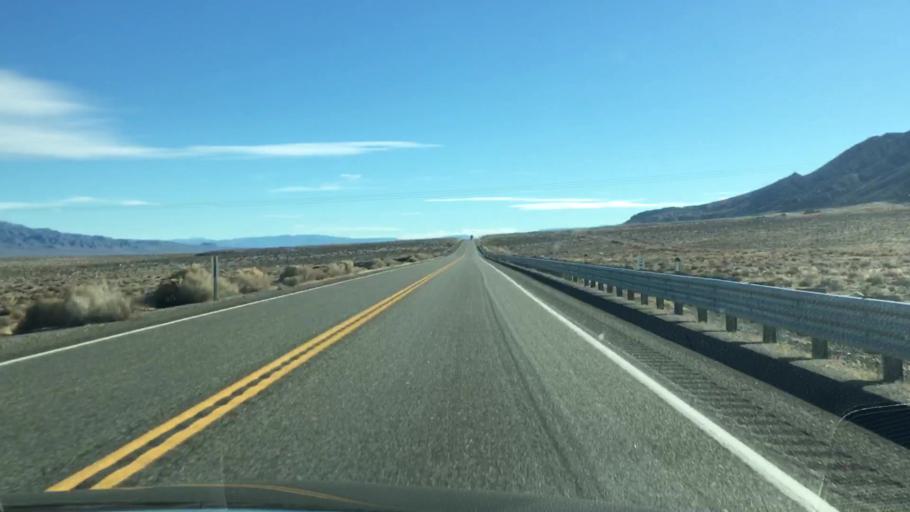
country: US
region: Nevada
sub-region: Mineral County
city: Hawthorne
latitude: 38.8126
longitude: -118.7656
